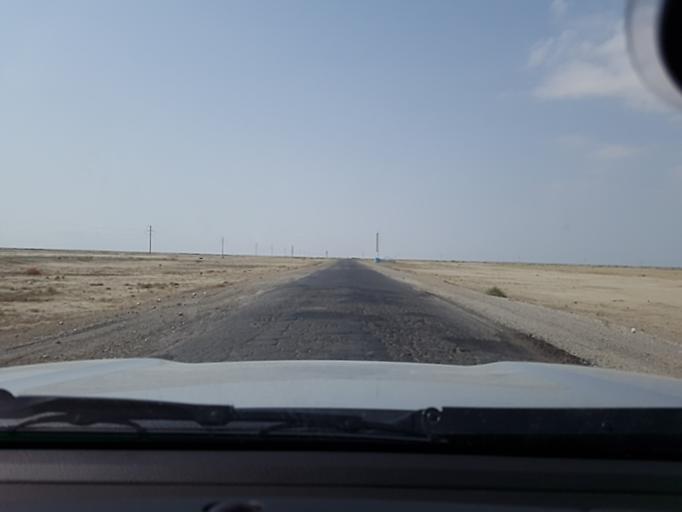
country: TM
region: Balkan
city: Gumdag
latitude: 39.0134
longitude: 54.5856
